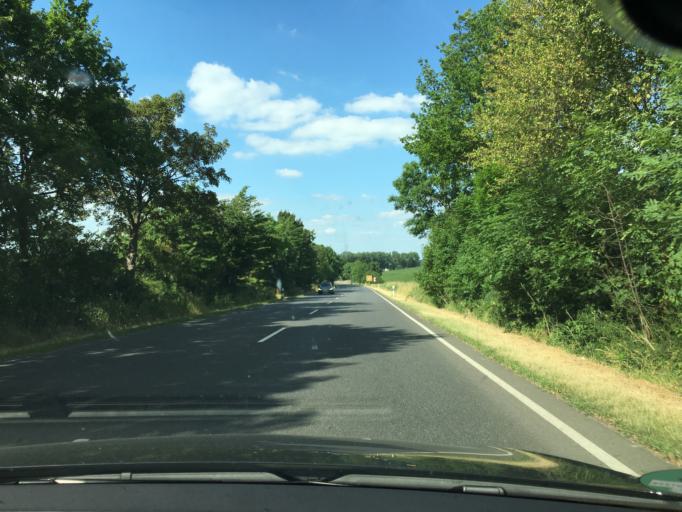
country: DE
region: North Rhine-Westphalia
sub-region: Regierungsbezirk Koln
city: Kreuzau
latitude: 50.7464
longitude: 6.4654
